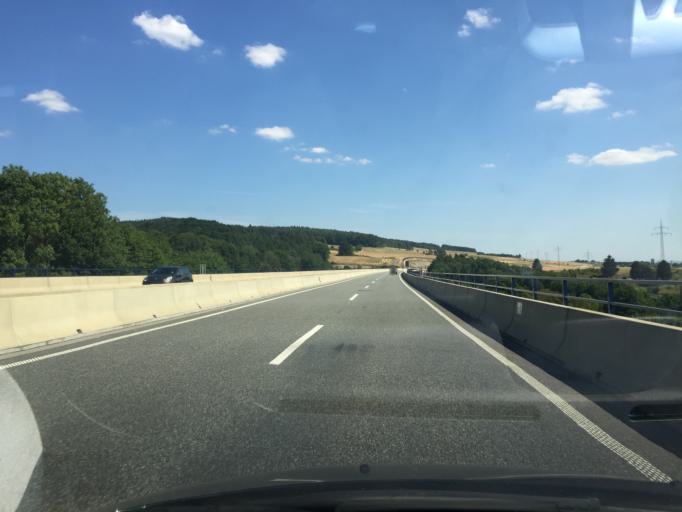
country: DE
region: Lower Saxony
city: Bad Lauterberg im Harz
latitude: 51.6086
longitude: 10.4698
